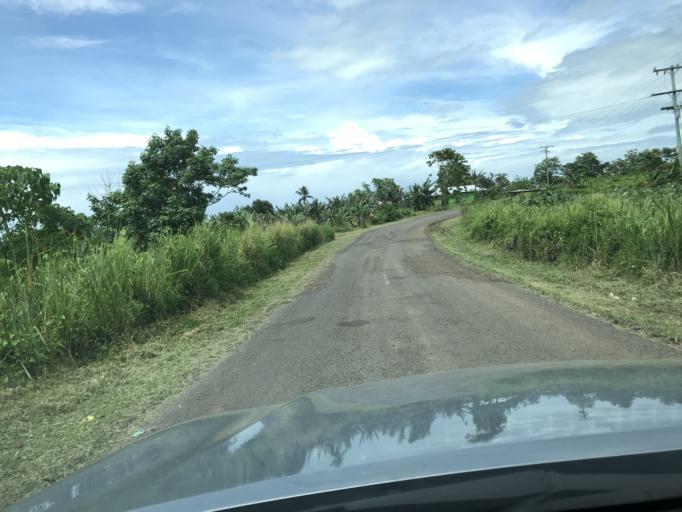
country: WS
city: Fasito`outa
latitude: -13.8601
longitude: -171.9093
